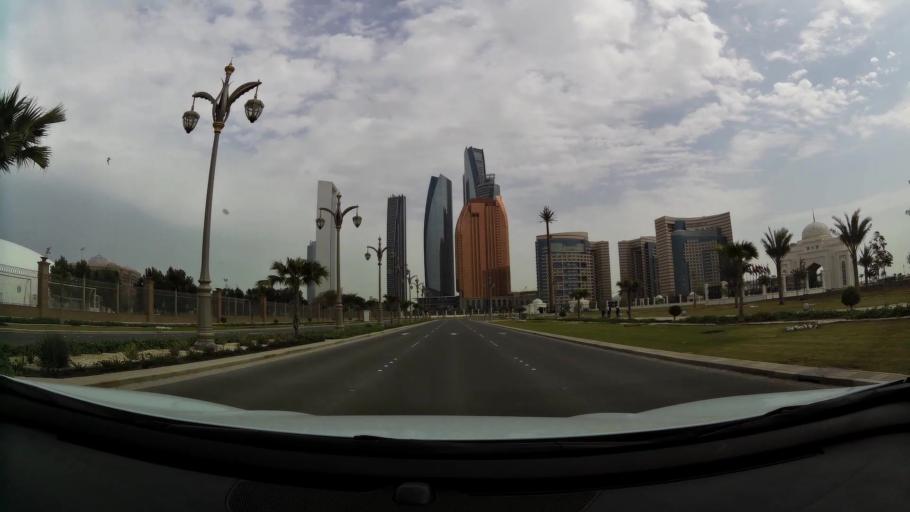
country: AE
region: Abu Dhabi
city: Abu Dhabi
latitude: 24.4573
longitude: 54.3140
